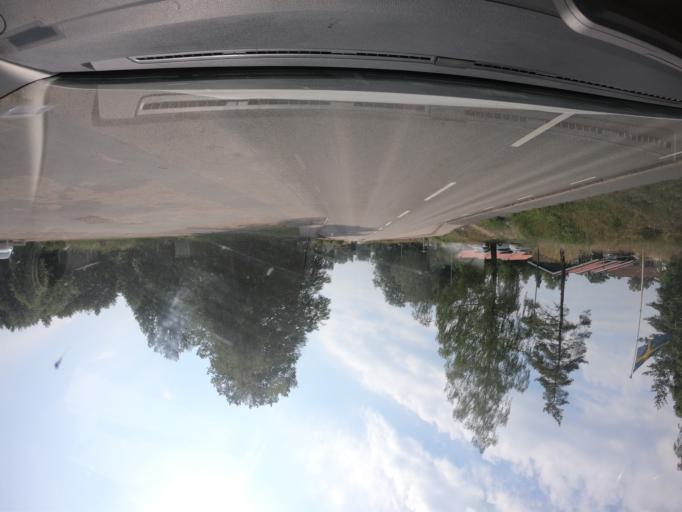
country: SE
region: Skane
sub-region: Hassleholms Kommun
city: Bjarnum
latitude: 56.3518
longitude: 13.6621
